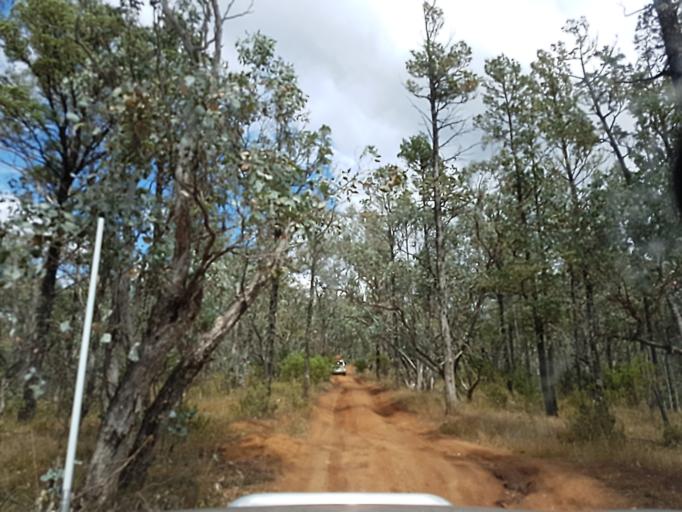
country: AU
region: New South Wales
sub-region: Snowy River
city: Jindabyne
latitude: -36.9290
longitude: 148.3977
